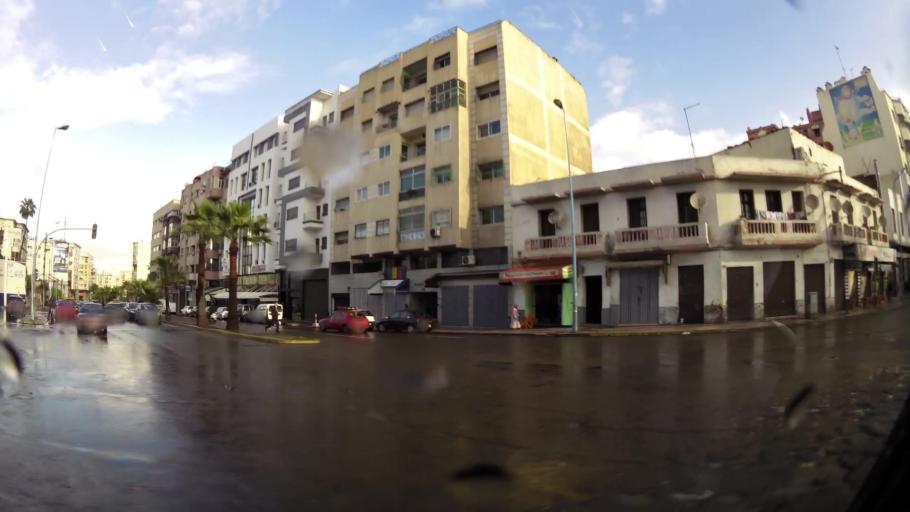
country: MA
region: Grand Casablanca
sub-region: Casablanca
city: Casablanca
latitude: 33.5870
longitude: -7.5946
